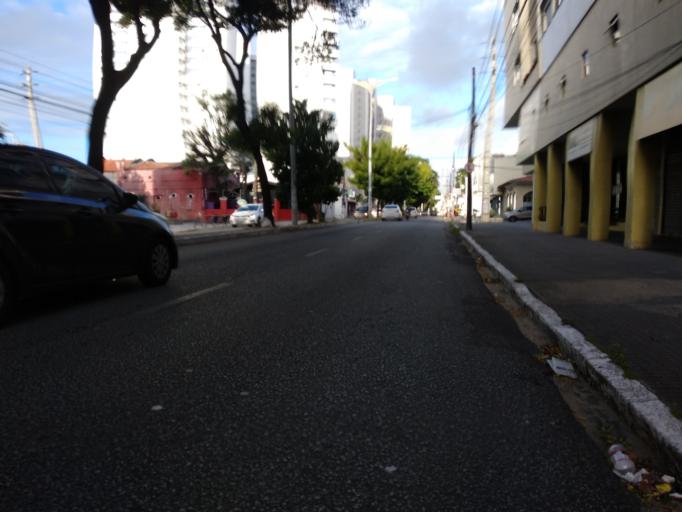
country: BR
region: Ceara
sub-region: Fortaleza
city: Fortaleza
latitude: -3.7341
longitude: -38.5227
